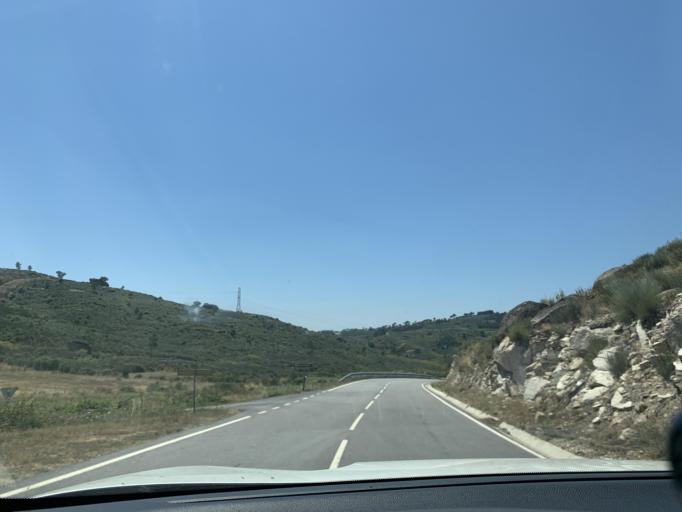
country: PT
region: Viseu
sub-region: Mangualde
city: Mangualde
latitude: 40.5710
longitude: -7.6488
